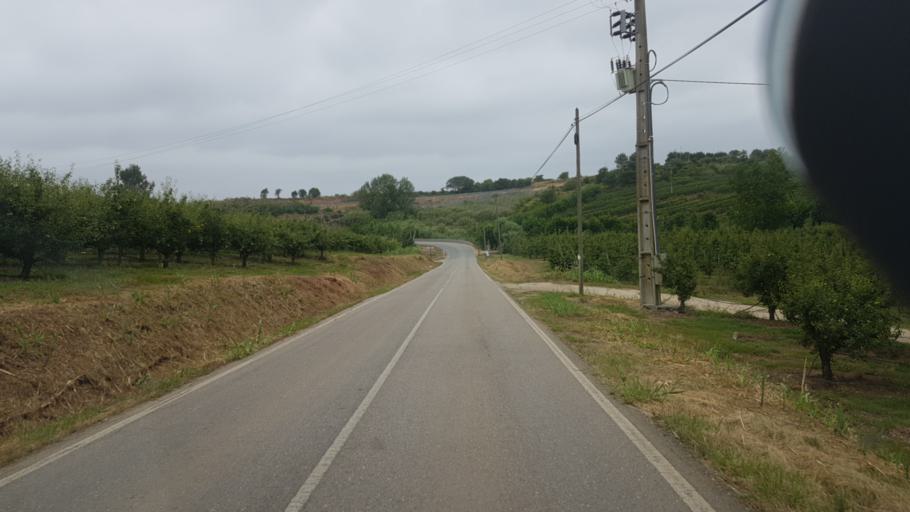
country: PT
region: Leiria
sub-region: Bombarral
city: Bombarral
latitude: 39.2726
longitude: -9.1711
